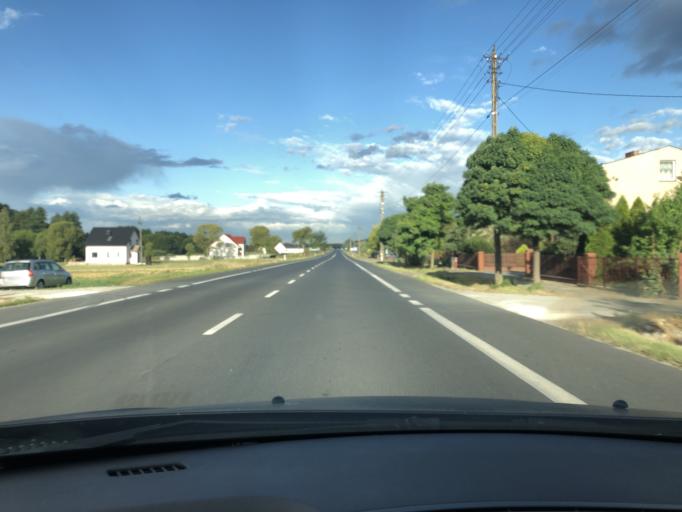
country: PL
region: Lodz Voivodeship
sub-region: Powiat wieruszowski
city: Galewice
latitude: 51.3036
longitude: 18.2696
